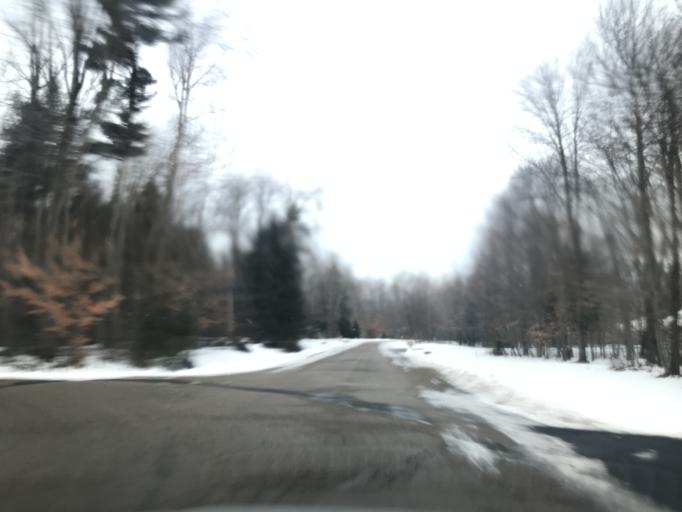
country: US
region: Wisconsin
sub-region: Brown County
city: Suamico
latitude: 44.6871
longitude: -88.0622
